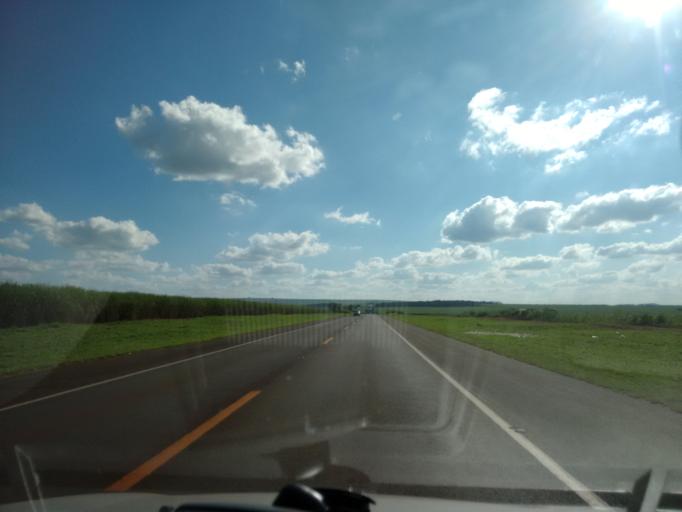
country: BR
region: Sao Paulo
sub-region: Americo Brasiliense
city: Americo Brasiliense
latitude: -21.6236
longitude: -47.9715
